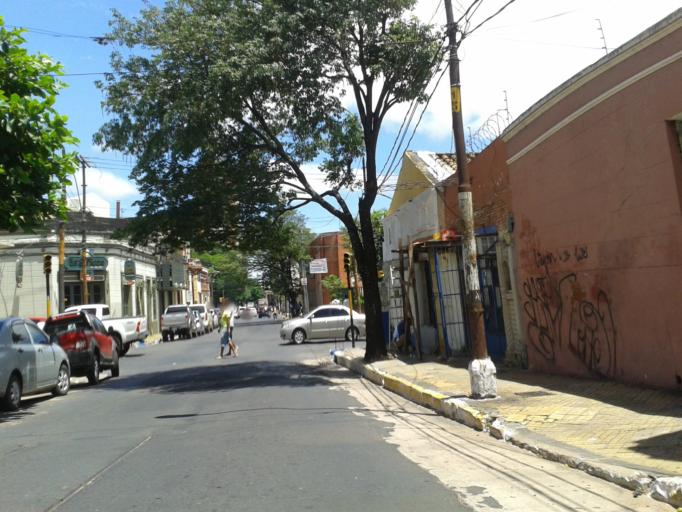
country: PY
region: Asuncion
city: Asuncion
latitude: -25.2853
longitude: -57.6276
